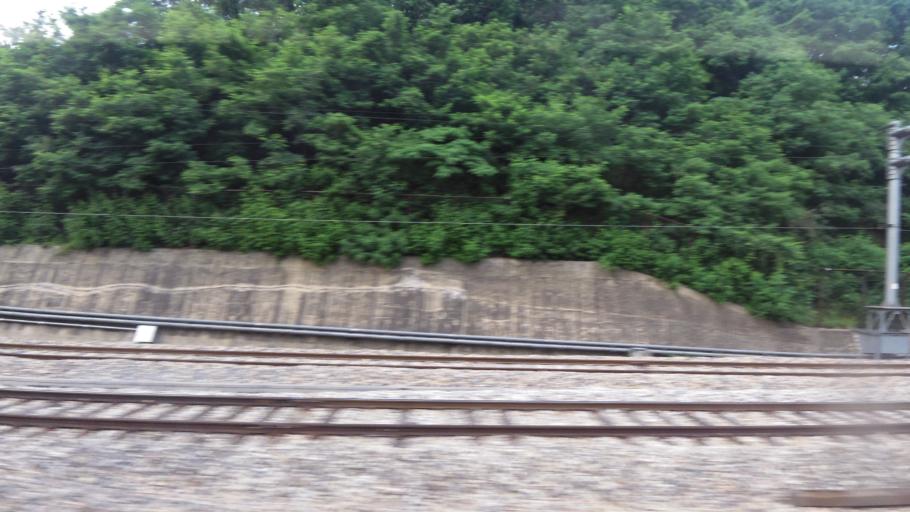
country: KR
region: Daejeon
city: Sintansin
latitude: 36.5013
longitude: 127.3883
